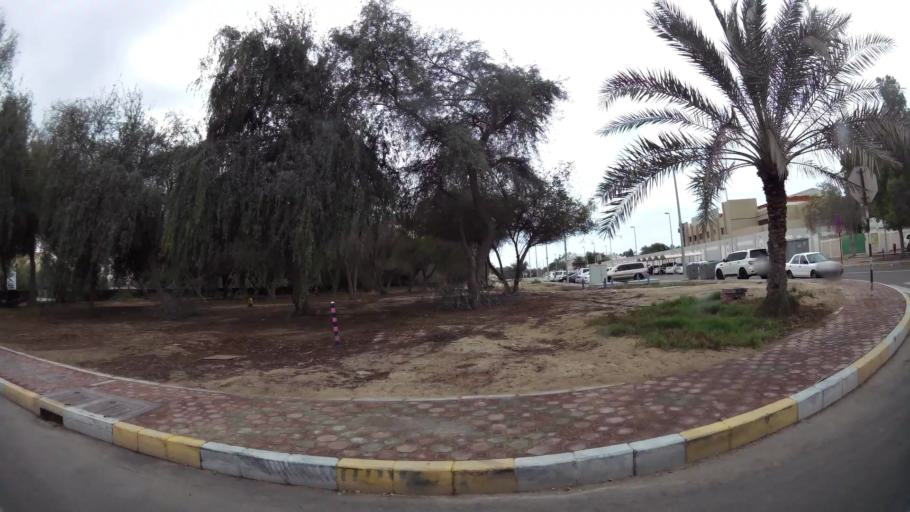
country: AE
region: Abu Dhabi
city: Abu Dhabi
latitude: 24.4296
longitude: 54.4259
